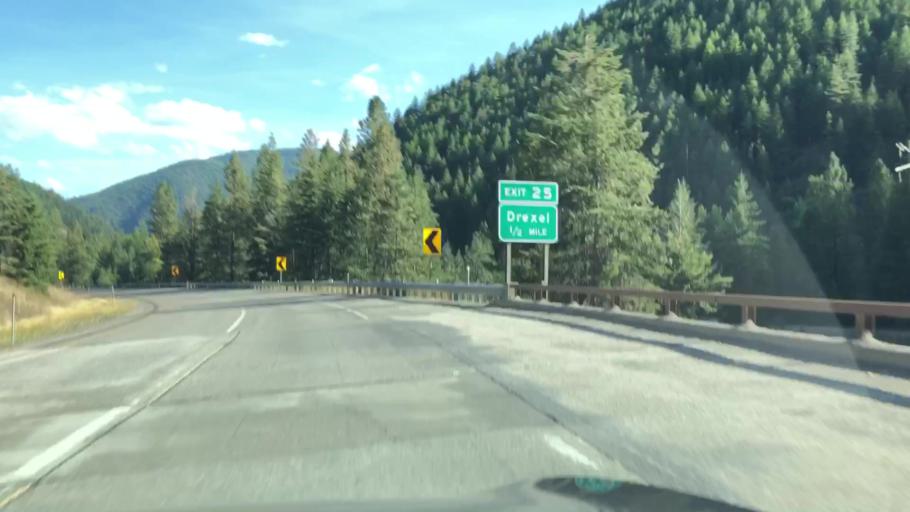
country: US
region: Montana
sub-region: Sanders County
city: Thompson Falls
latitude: 47.3285
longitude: -115.2575
